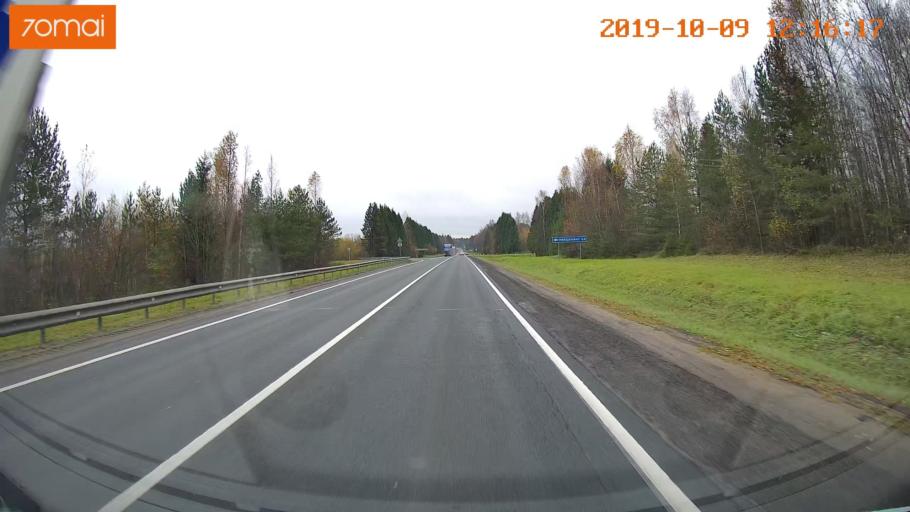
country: RU
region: Jaroslavl
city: Prechistoye
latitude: 58.4708
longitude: 40.3214
